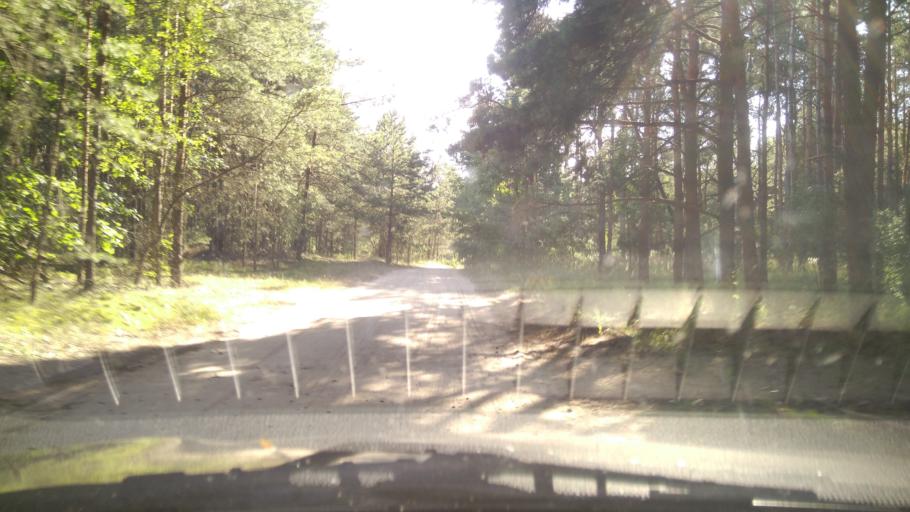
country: BY
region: Brest
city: Byelaazyorsk
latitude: 52.4456
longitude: 25.1633
